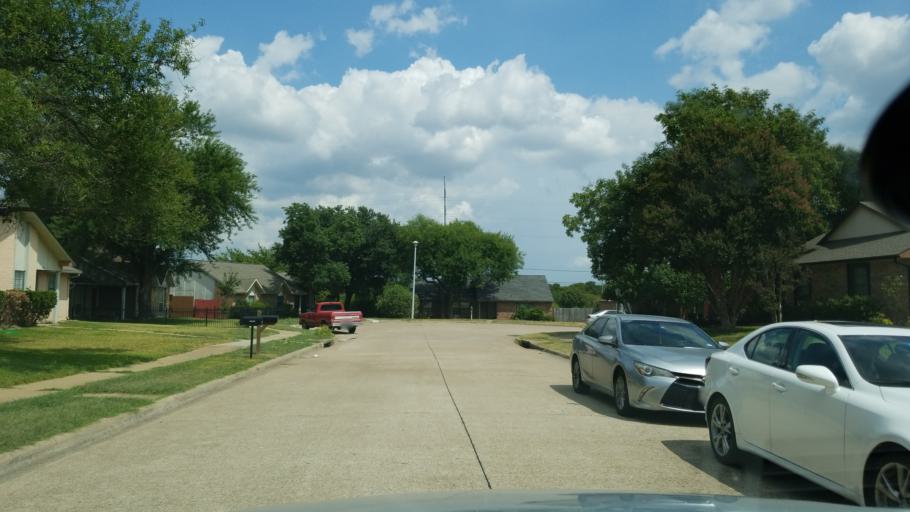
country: US
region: Texas
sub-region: Dallas County
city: Garland
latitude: 32.9225
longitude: -96.6666
